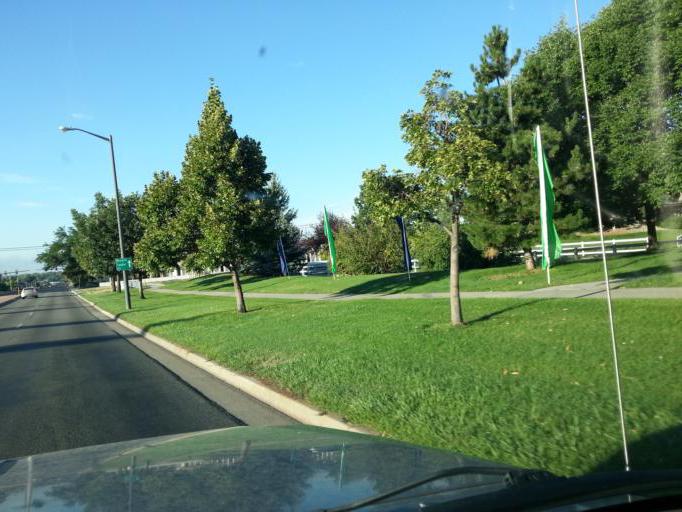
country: US
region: Colorado
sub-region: Larimer County
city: Loveland
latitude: 40.4053
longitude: -105.1105
